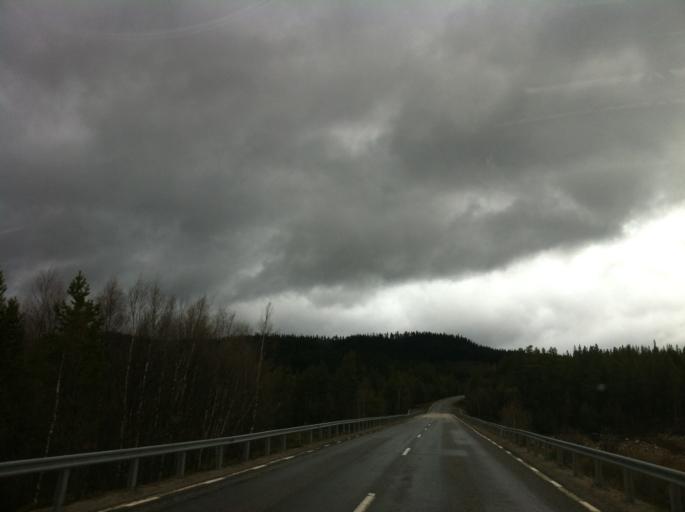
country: NO
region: Hedmark
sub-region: Engerdal
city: Engerdal
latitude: 62.4246
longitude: 12.7441
